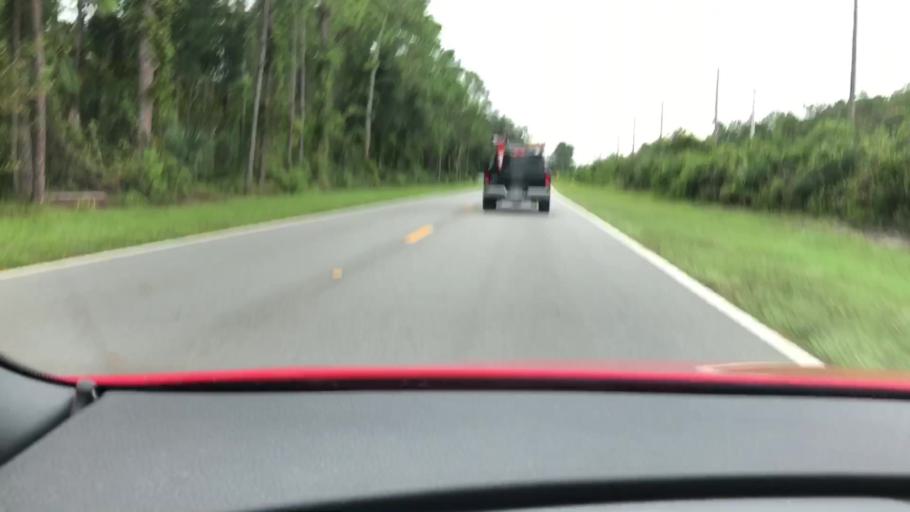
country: US
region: Florida
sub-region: Flagler County
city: Palm Coast
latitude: 29.5141
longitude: -81.1961
